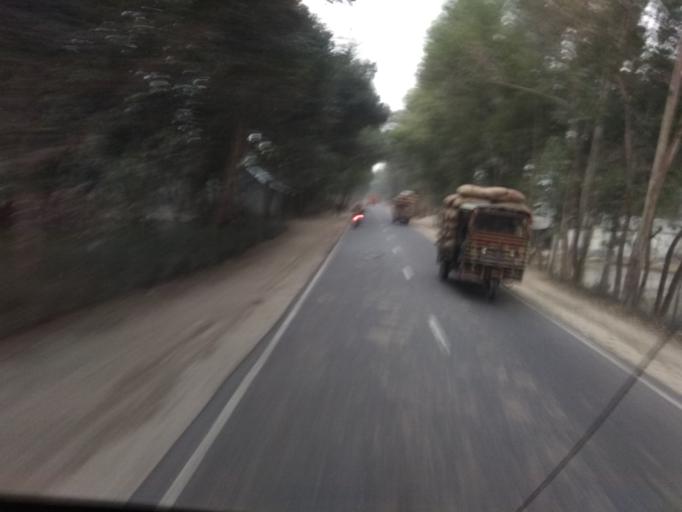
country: BD
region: Rajshahi
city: Bogra
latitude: 24.6801
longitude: 89.2866
